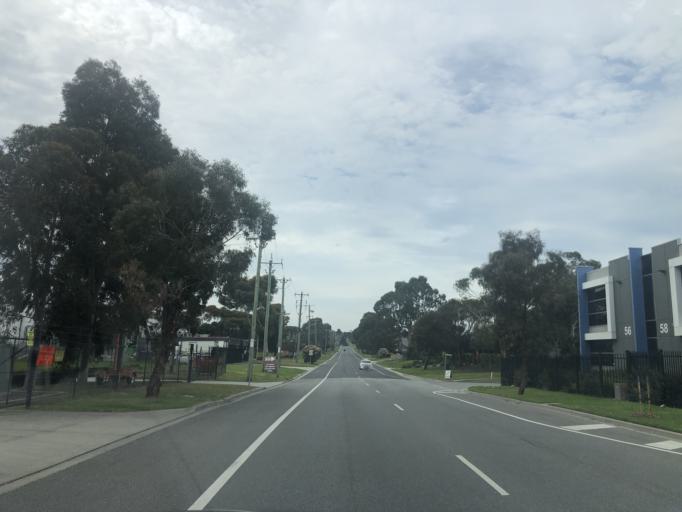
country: AU
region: Victoria
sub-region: Casey
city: Hallam
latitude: -38.0124
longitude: 145.2550
